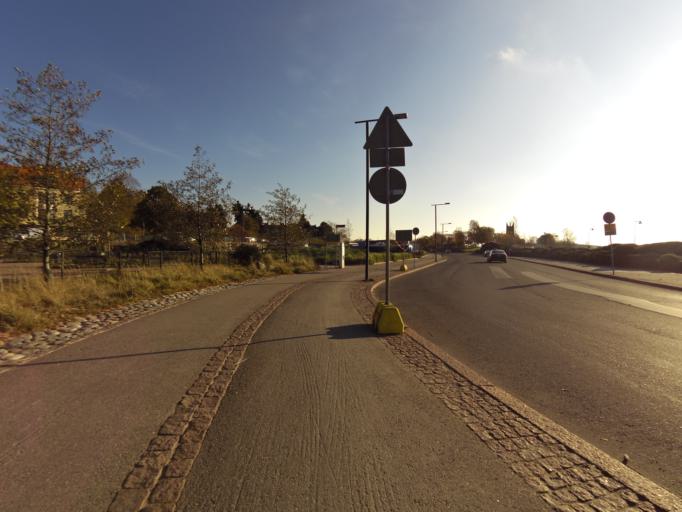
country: FI
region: Uusimaa
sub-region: Helsinki
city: Helsinki
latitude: 60.1551
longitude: 24.9351
